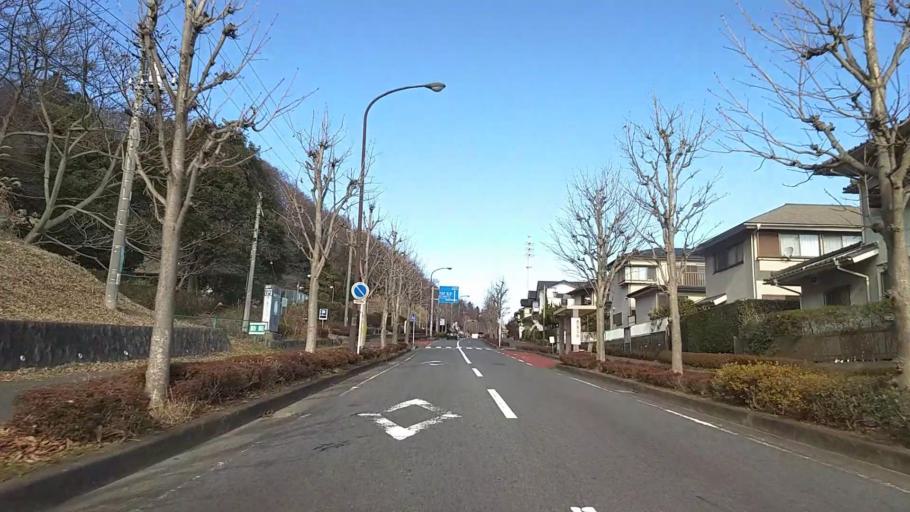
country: JP
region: Kanagawa
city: Atsugi
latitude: 35.4461
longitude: 139.3050
